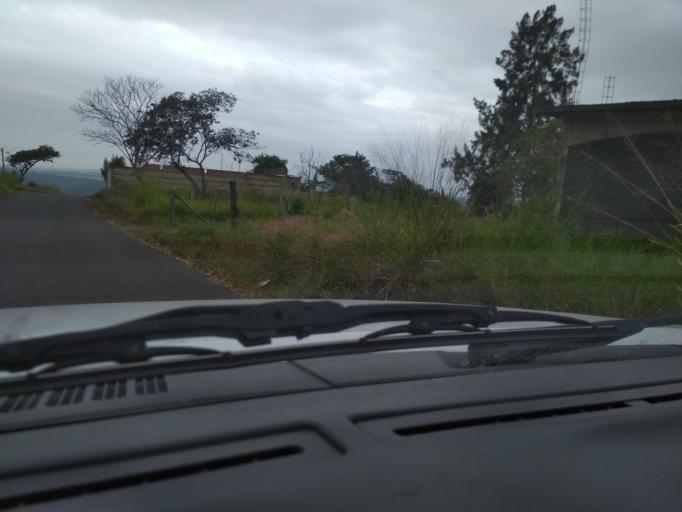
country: MX
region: Veracruz
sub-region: Emiliano Zapata
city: Dos Rios
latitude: 19.5169
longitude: -96.7931
